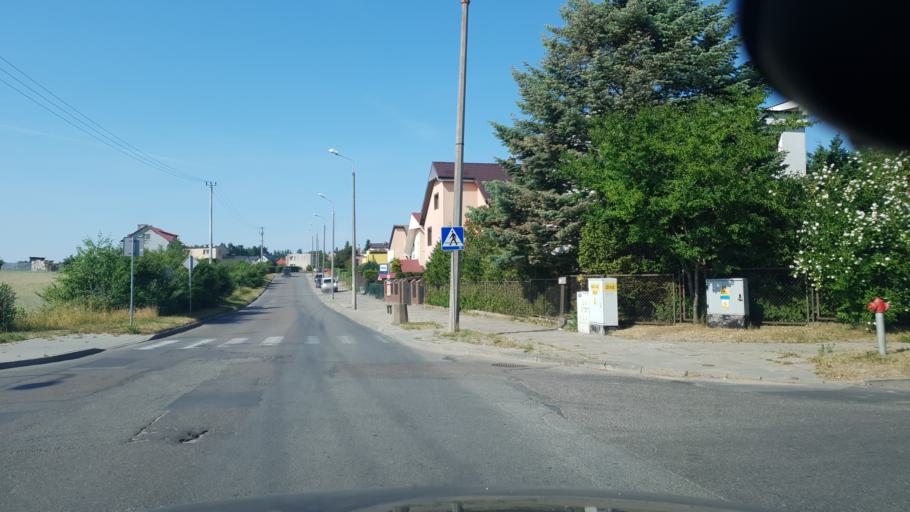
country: PL
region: Pomeranian Voivodeship
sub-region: Powiat kartuski
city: Chwaszczyno
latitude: 54.4278
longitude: 18.4607
